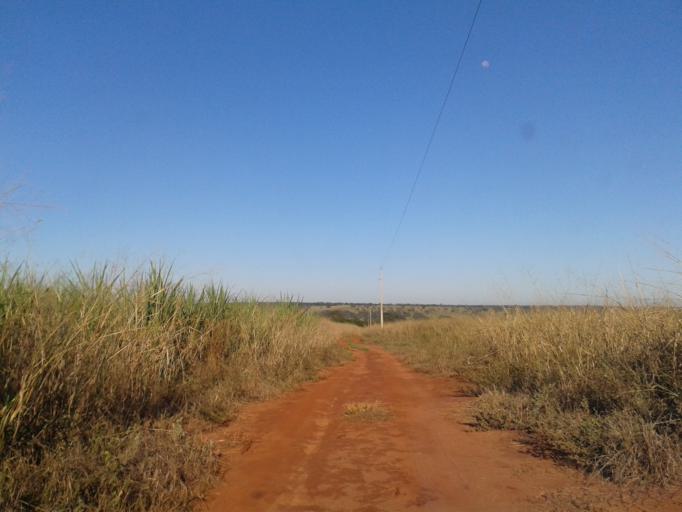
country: BR
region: Minas Gerais
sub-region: Santa Vitoria
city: Santa Vitoria
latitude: -19.0219
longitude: -50.3633
